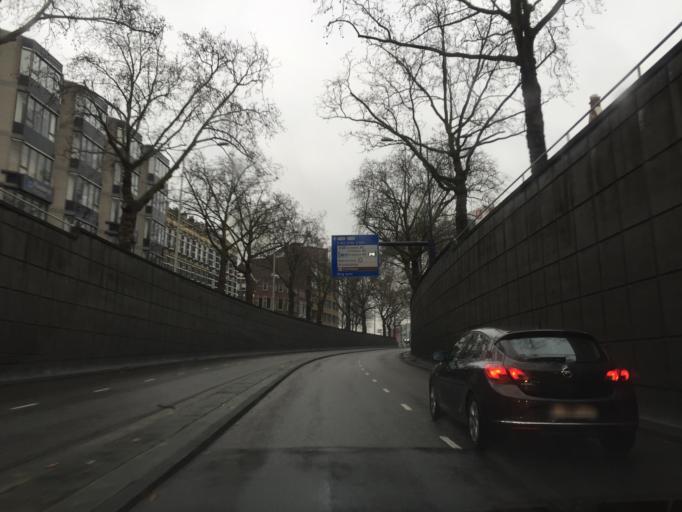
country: NL
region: South Holland
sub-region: Gemeente Rotterdam
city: Delfshaven
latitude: 51.9138
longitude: 4.4636
